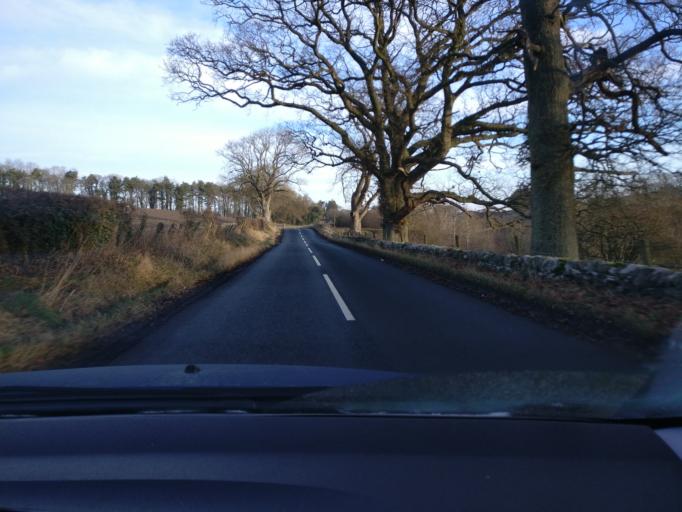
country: GB
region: Scotland
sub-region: The Scottish Borders
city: Hawick
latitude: 55.4424
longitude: -2.7695
